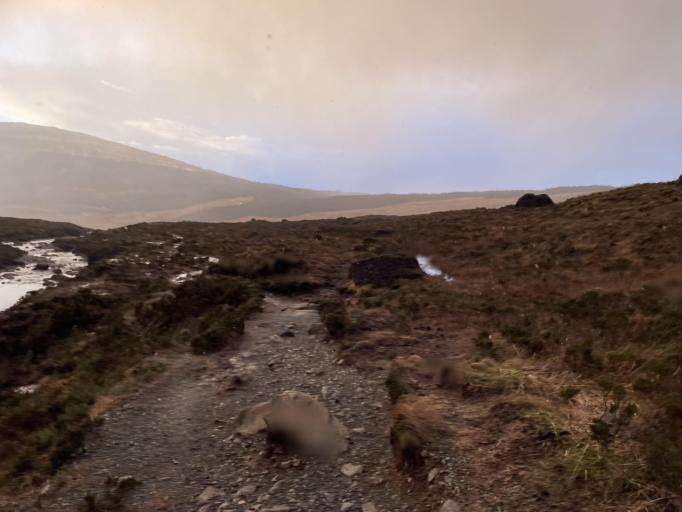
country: GB
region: Scotland
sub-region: Highland
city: Isle of Skye
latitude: 57.2490
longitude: -6.2448
